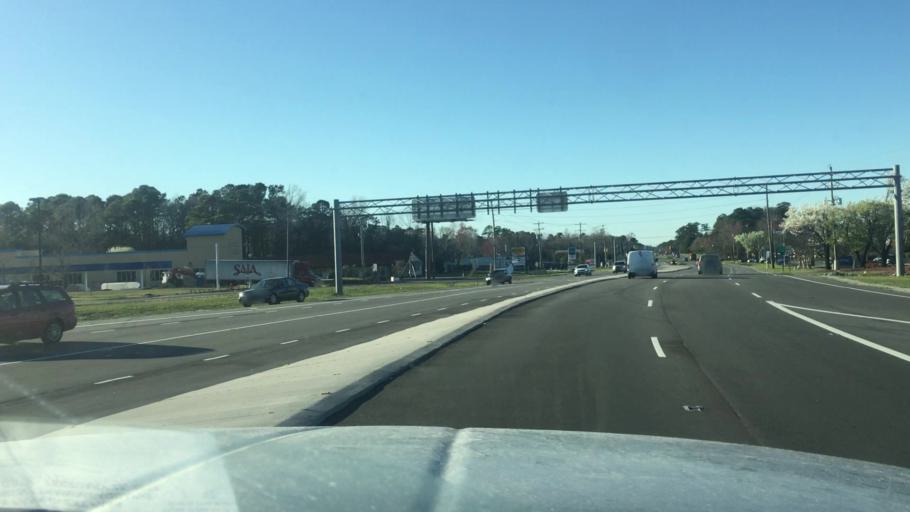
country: US
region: North Carolina
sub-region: New Hanover County
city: Myrtle Grove
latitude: 34.1406
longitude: -77.8942
